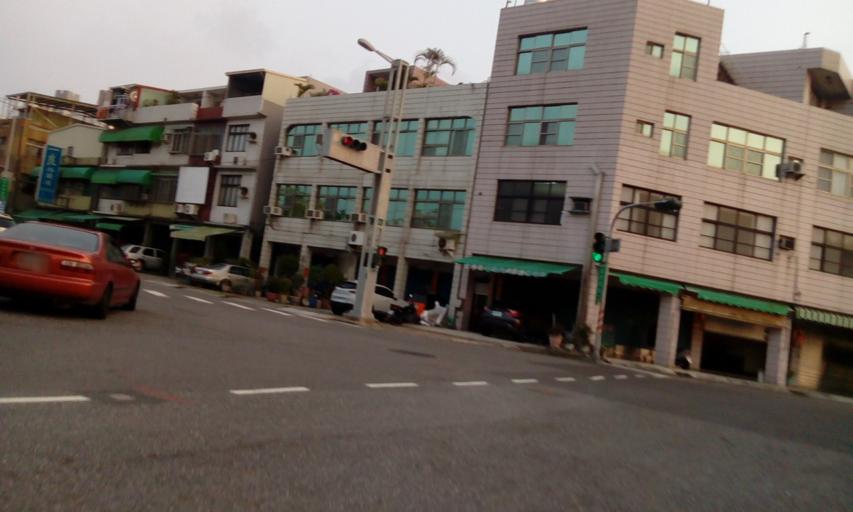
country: TW
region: Kaohsiung
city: Kaohsiung
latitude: 22.6882
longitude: 120.3035
